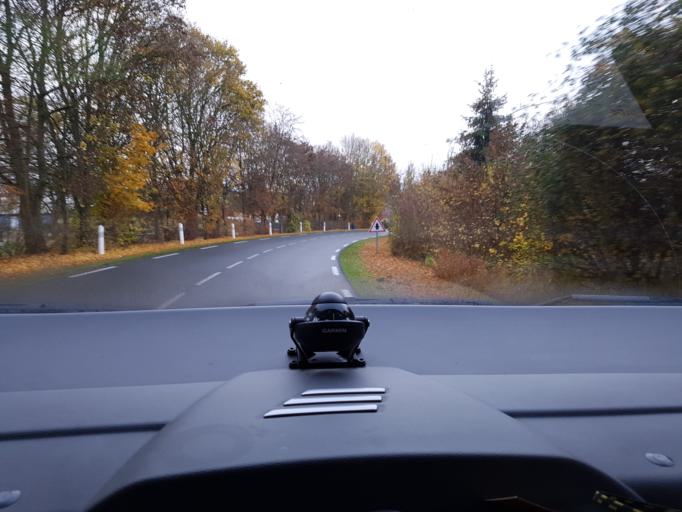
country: FR
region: Haute-Normandie
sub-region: Departement de la Seine-Maritime
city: Duclair
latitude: 49.4871
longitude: 0.8879
